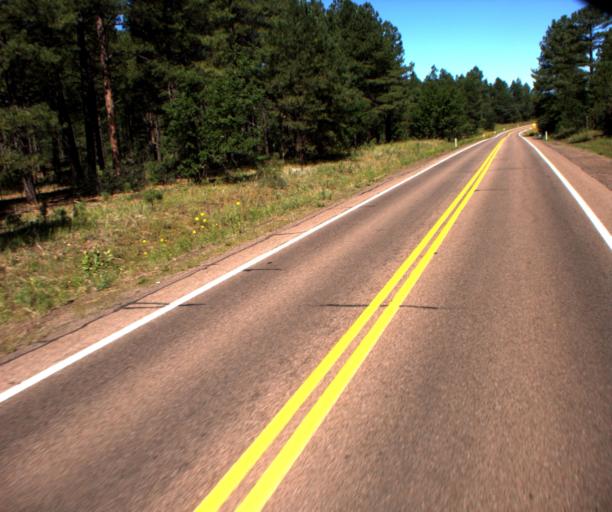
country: US
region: Arizona
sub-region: Navajo County
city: Pinetop-Lakeside
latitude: 34.0774
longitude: -109.8658
